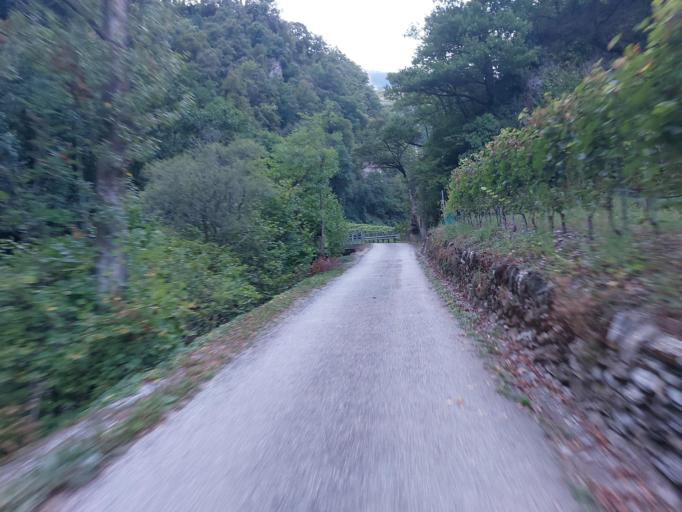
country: CH
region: Valais
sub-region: Conthey District
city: Conthey
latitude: 46.2417
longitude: 7.3101
